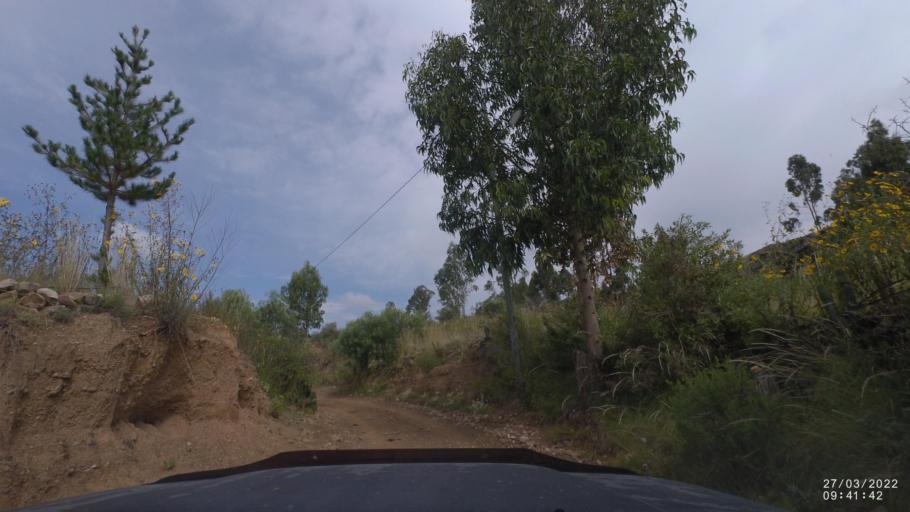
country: BO
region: Cochabamba
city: Cliza
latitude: -17.7517
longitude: -65.9007
